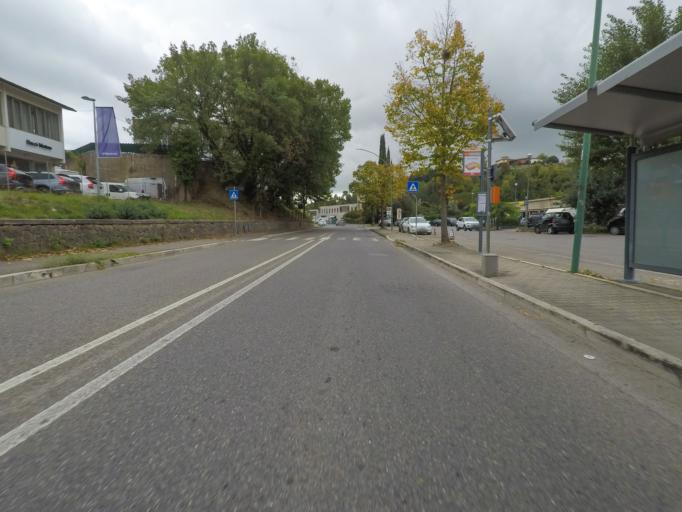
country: IT
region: Tuscany
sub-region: Provincia di Siena
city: Siena
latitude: 43.3203
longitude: 11.3506
